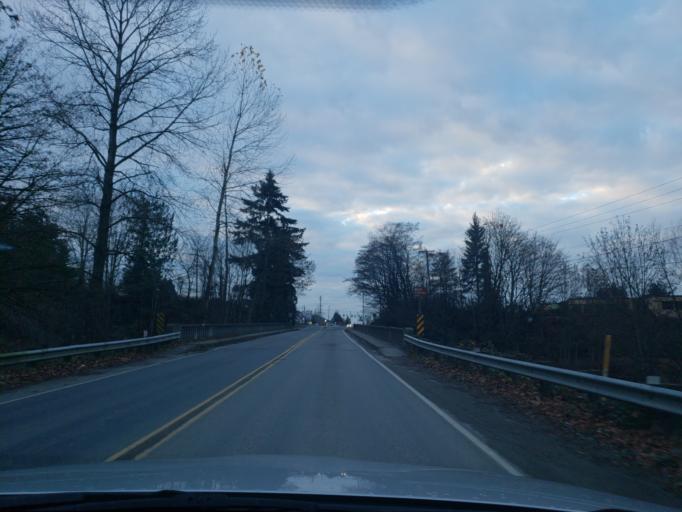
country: US
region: Washington
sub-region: Snohomish County
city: Snohomish
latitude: 47.9131
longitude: -122.0825
